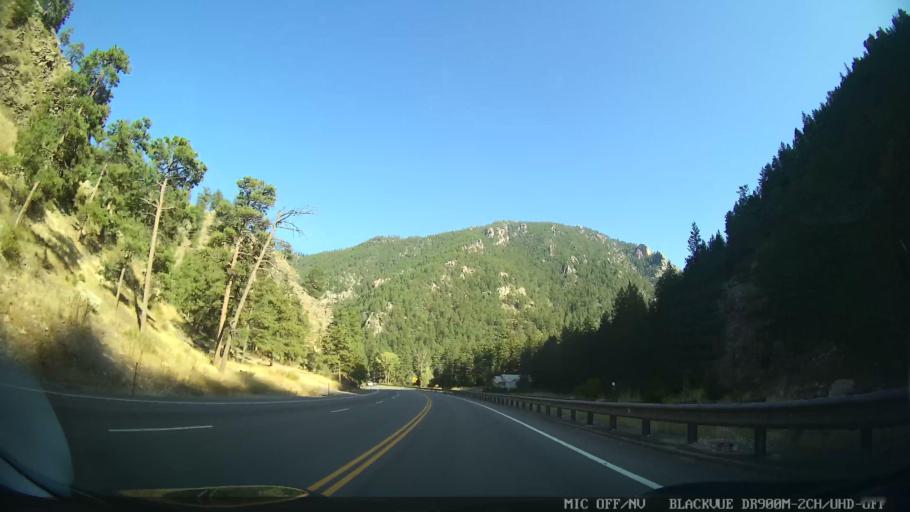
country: US
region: Colorado
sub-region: Larimer County
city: Estes Park
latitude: 40.4144
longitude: -105.3672
